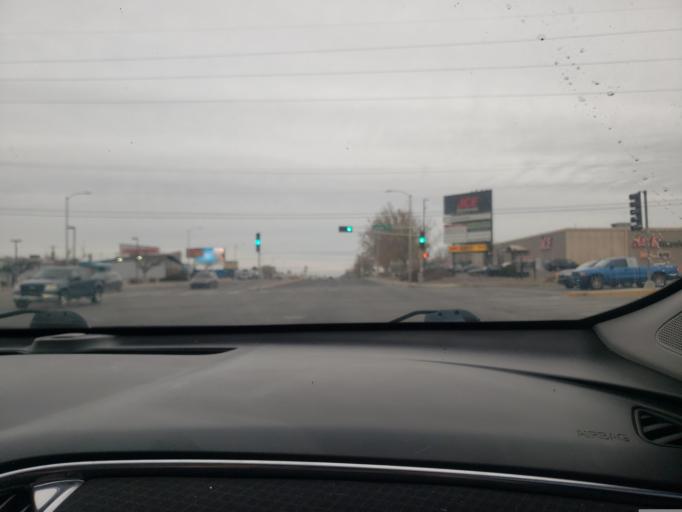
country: US
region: New Mexico
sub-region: Bernalillo County
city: Albuquerque
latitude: 35.0872
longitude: -106.5861
